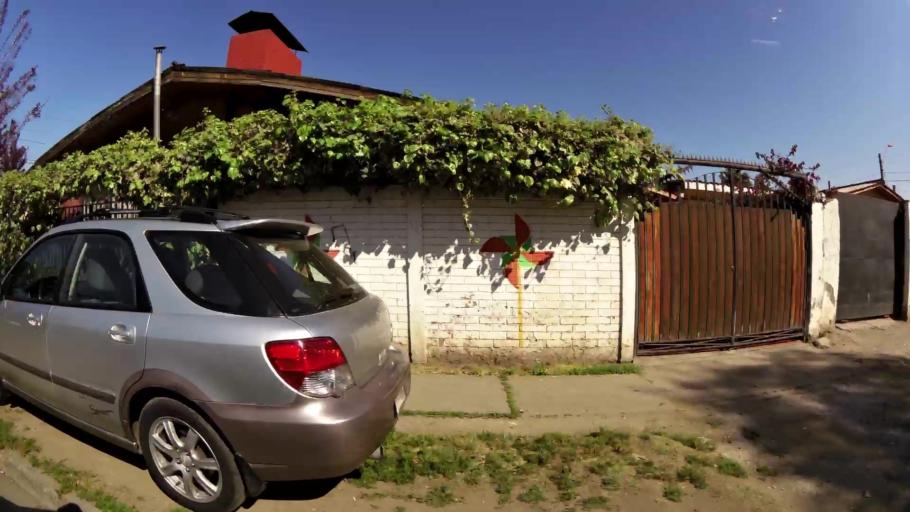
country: CL
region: Santiago Metropolitan
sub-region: Provincia de Chacabuco
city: Chicureo Abajo
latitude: -33.3591
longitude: -70.6895
